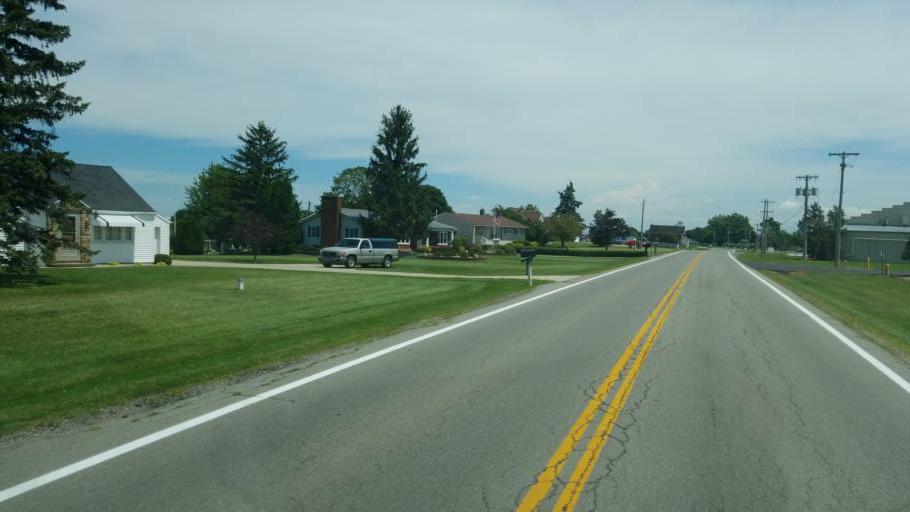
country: US
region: Ohio
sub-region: Richland County
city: Shelby
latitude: 40.8769
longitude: -82.6992
